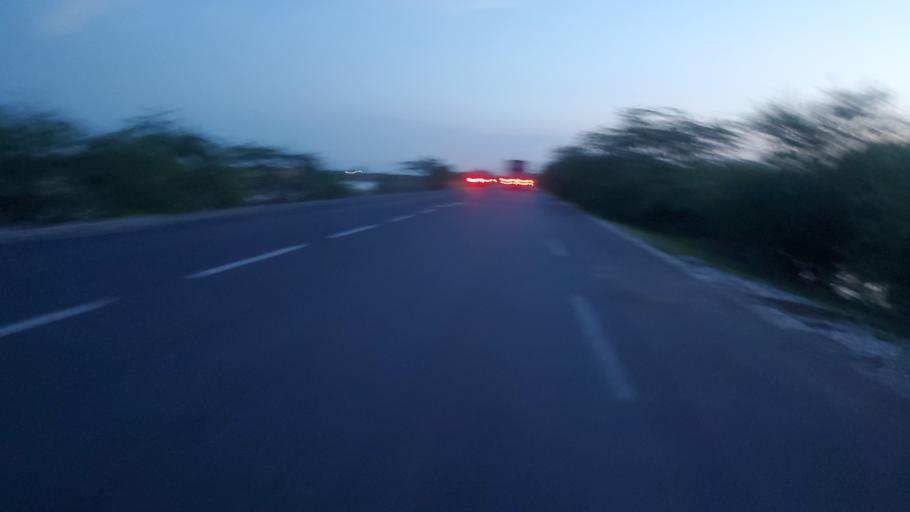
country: SN
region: Saint-Louis
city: Saint-Louis
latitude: 16.0661
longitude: -16.3928
